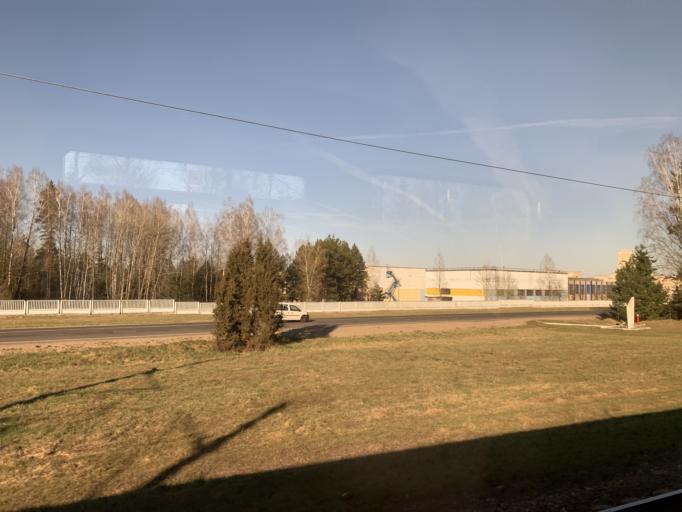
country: BY
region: Grodnenskaya
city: Smarhon'
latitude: 54.4391
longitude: 26.5074
